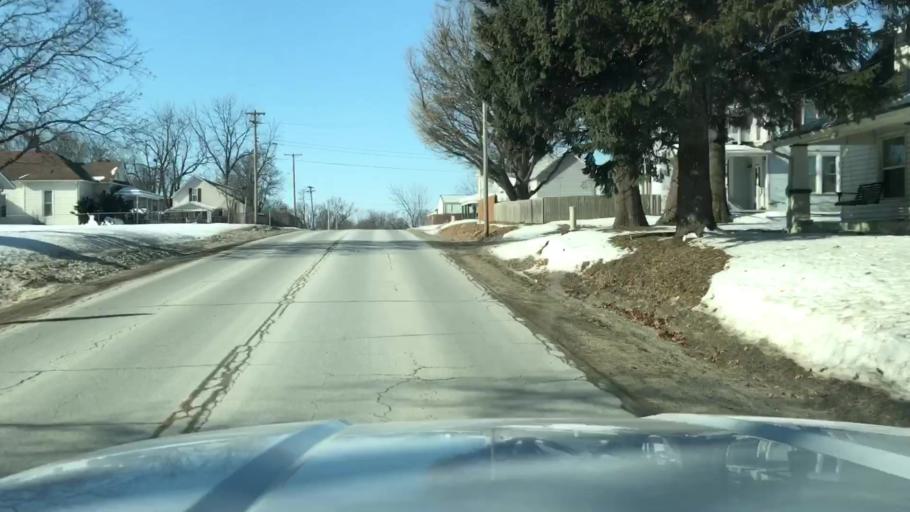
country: US
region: Missouri
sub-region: Andrew County
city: Savannah
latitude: 39.9470
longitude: -94.8355
